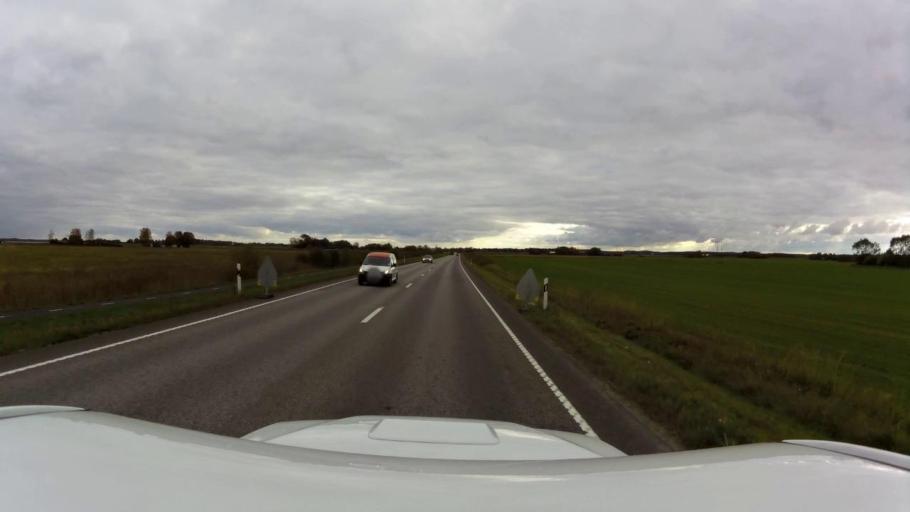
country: SE
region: OEstergoetland
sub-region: Linkopings Kommun
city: Berg
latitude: 58.4609
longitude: 15.5424
